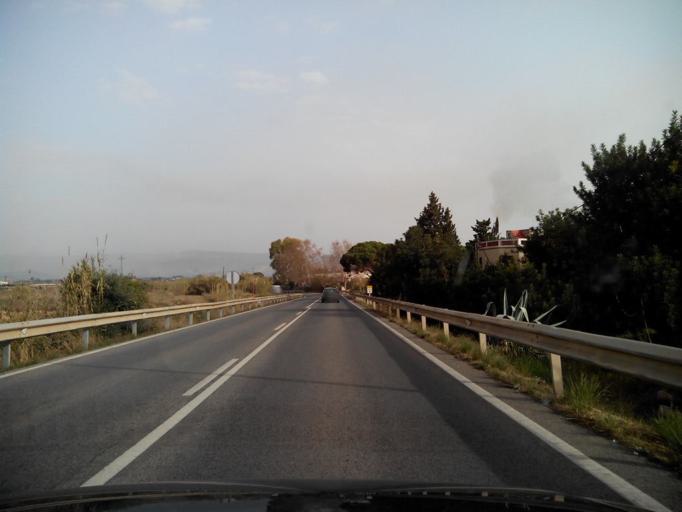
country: ES
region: Catalonia
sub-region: Provincia de Tarragona
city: Cambrils
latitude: 41.0979
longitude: 1.0828
